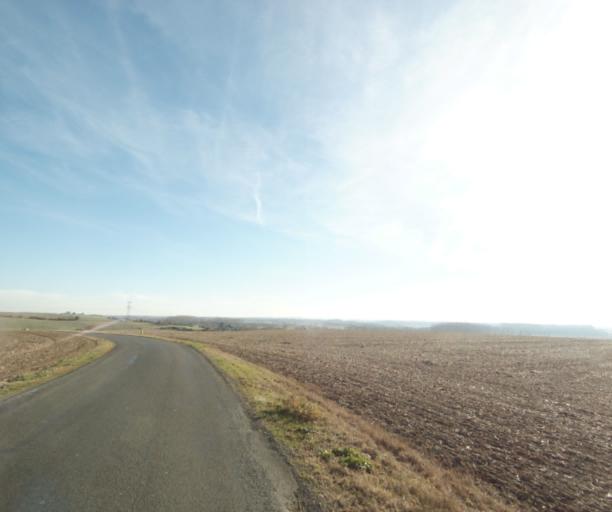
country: FR
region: Poitou-Charentes
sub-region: Departement de la Charente-Maritime
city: Les Gonds
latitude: 45.7329
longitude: -0.5930
